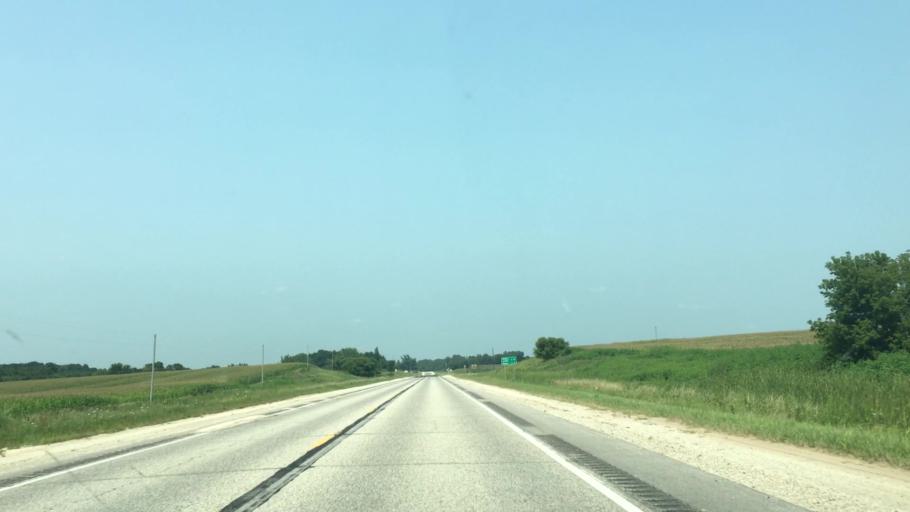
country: US
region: Iowa
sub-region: Fayette County
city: Fayette
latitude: 42.8149
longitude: -91.8051
